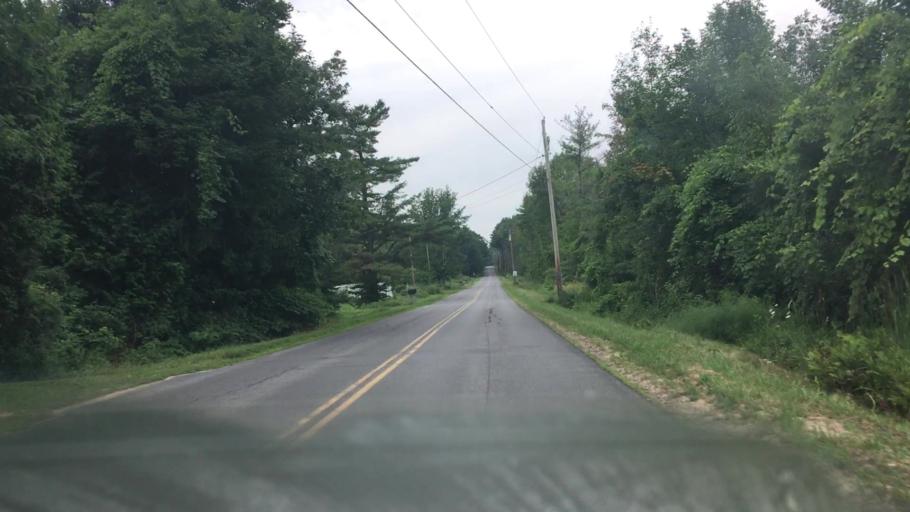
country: US
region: New York
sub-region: Clinton County
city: Morrisonville
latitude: 44.6426
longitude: -73.5695
